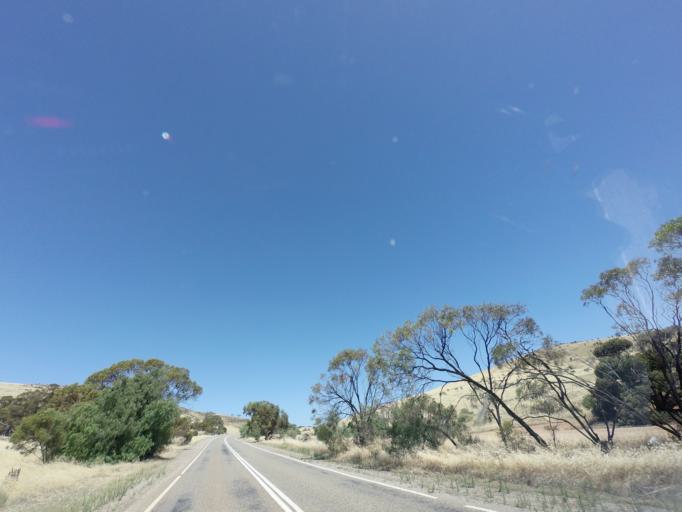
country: AU
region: South Australia
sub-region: Peterborough
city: Peterborough
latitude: -32.7342
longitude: 138.5383
